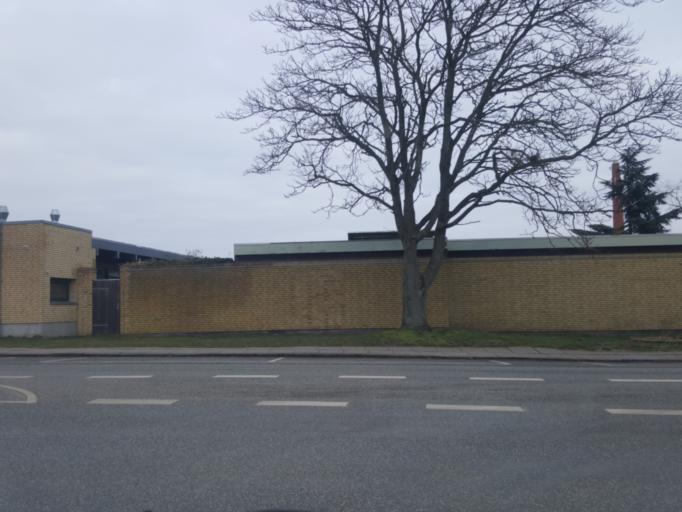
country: DK
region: Zealand
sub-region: Vordingborg Kommune
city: Vordingborg
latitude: 55.0108
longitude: 11.9083
